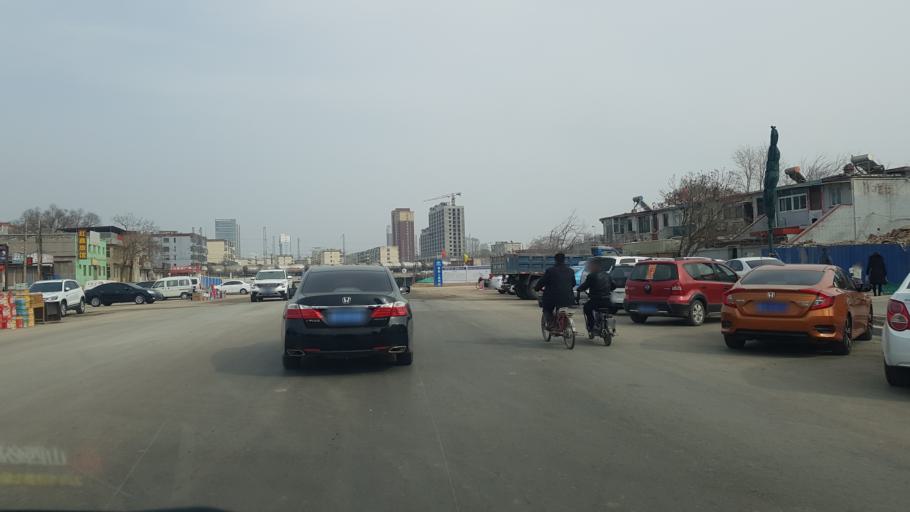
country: CN
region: Shanxi Sheng
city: Yuci
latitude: 37.6902
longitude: 112.7279
